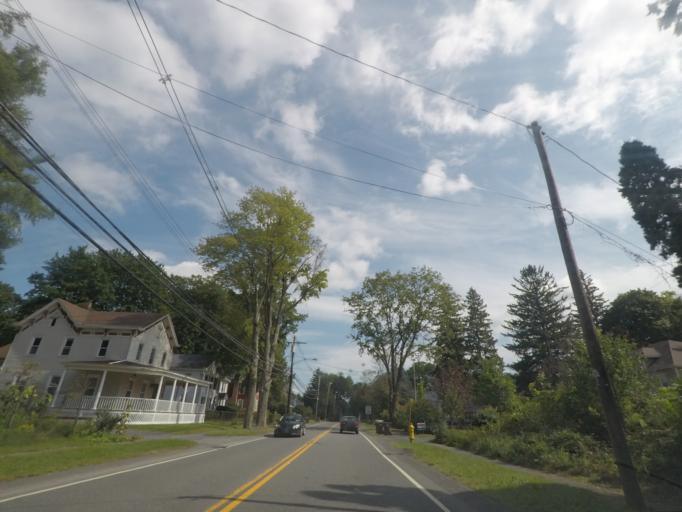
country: US
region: New York
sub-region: Albany County
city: Delmar
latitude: 42.6237
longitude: -73.8407
